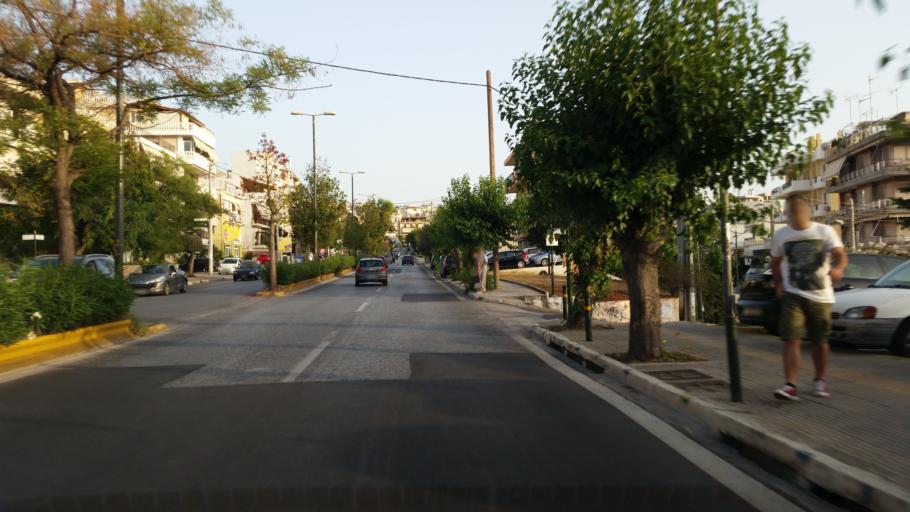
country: GR
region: Attica
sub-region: Nomarchia Athinas
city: Ilioupoli
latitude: 37.9321
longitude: 23.7589
